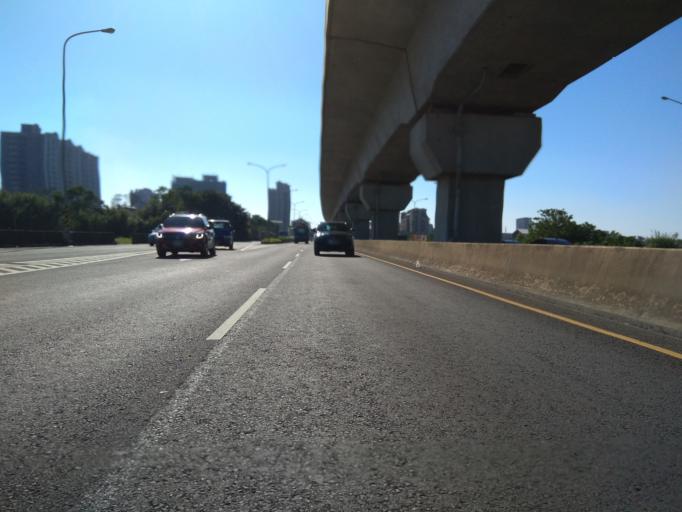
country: TW
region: Taiwan
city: Taoyuan City
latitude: 24.9657
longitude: 121.1676
